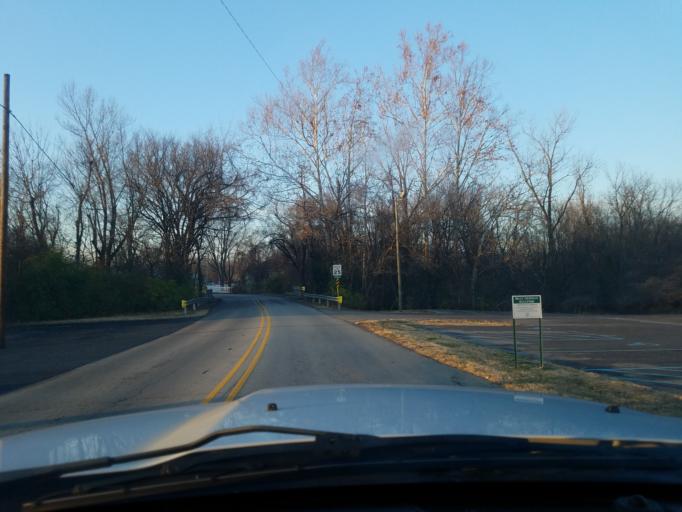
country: US
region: Indiana
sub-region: Floyd County
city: New Albany
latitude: 38.2875
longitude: -85.8274
